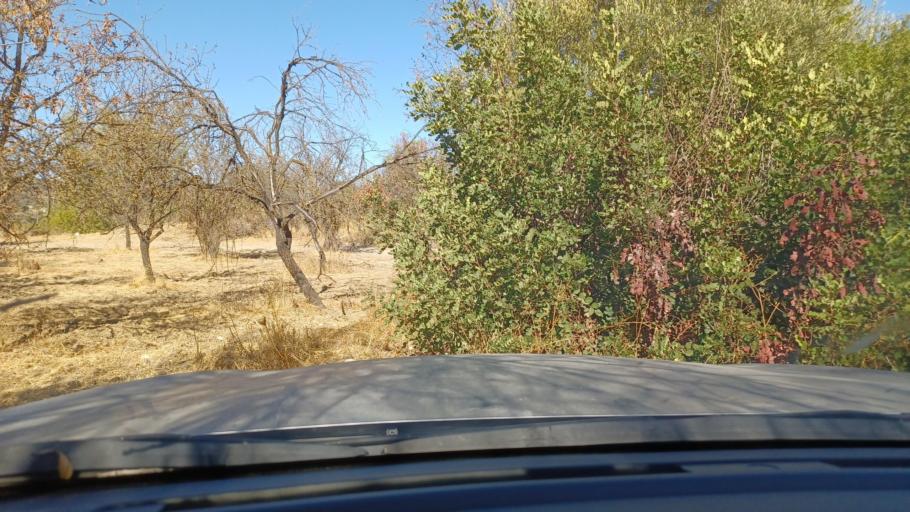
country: CY
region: Pafos
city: Polis
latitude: 35.0073
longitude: 32.5066
